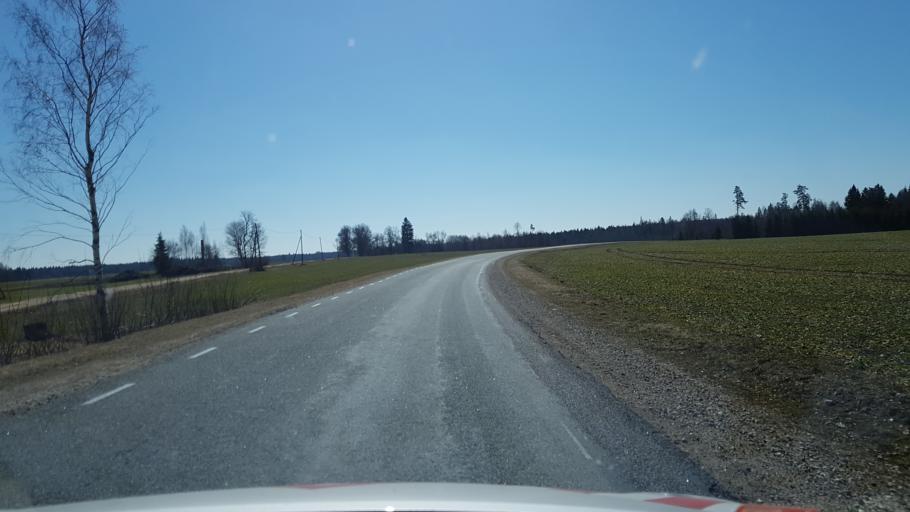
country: EE
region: Laeaene-Virumaa
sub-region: Rakke vald
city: Rakke
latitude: 59.0228
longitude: 26.3532
